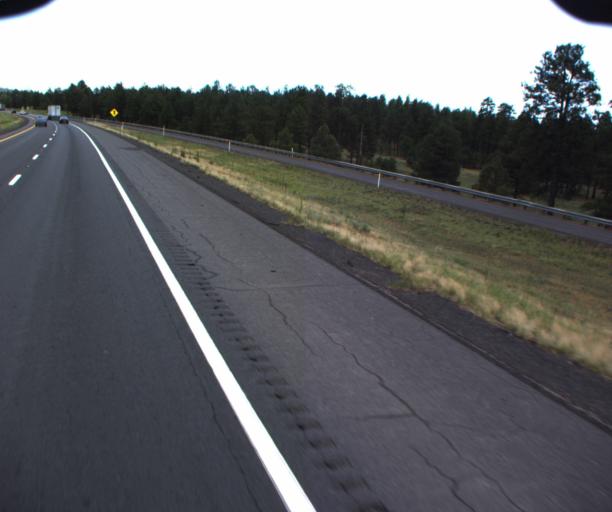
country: US
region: Arizona
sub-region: Coconino County
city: Williams
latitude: 35.2594
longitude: -112.1487
